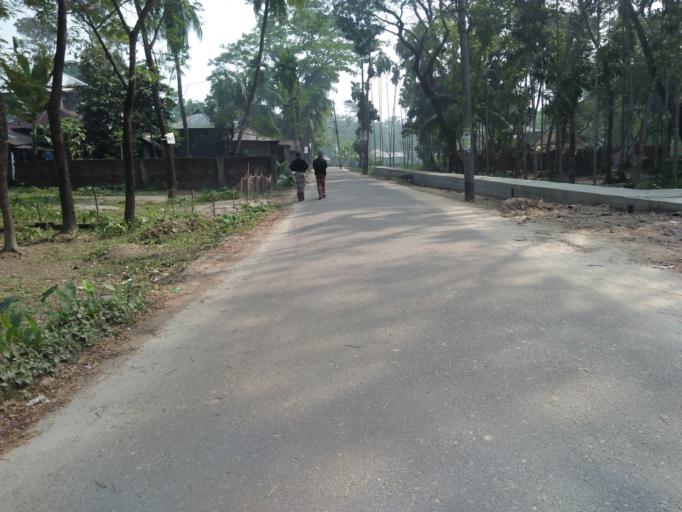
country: BD
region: Barisal
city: Bhola
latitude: 22.6800
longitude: 90.6380
